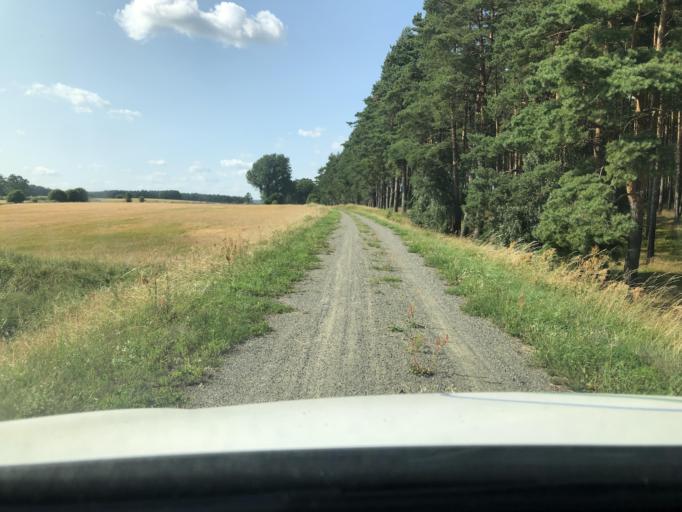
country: SE
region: Skane
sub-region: Kristianstads Kommun
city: Degeberga
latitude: 55.8142
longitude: 14.1291
